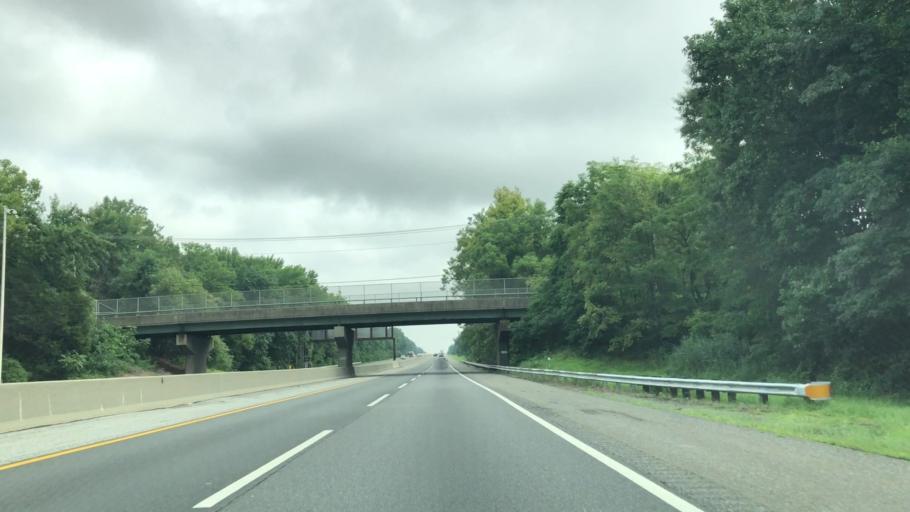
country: US
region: New Jersey
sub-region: Gloucester County
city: Mullica Hill
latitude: 39.7797
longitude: -75.2313
